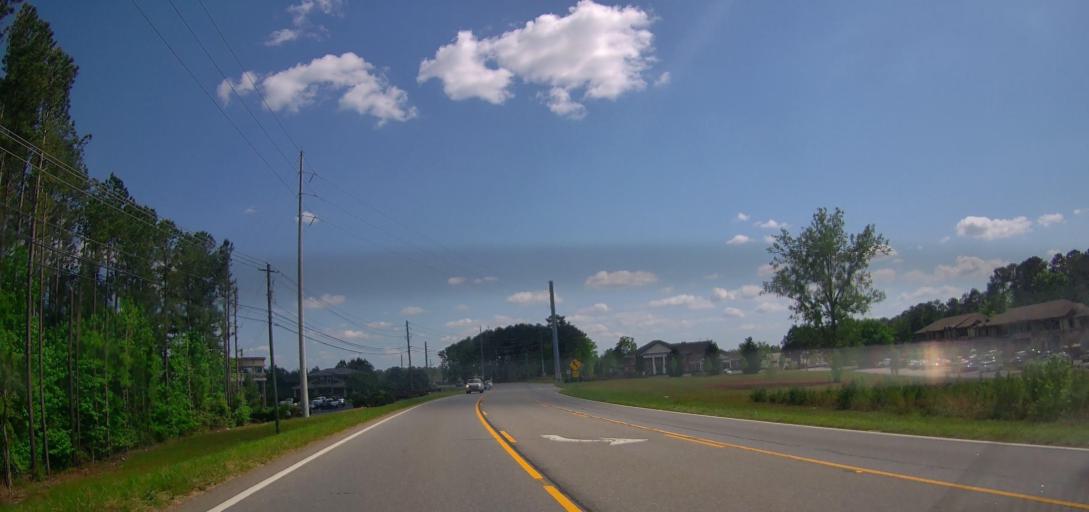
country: US
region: Georgia
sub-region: Putnam County
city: Jefferson
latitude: 33.4682
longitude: -83.2444
